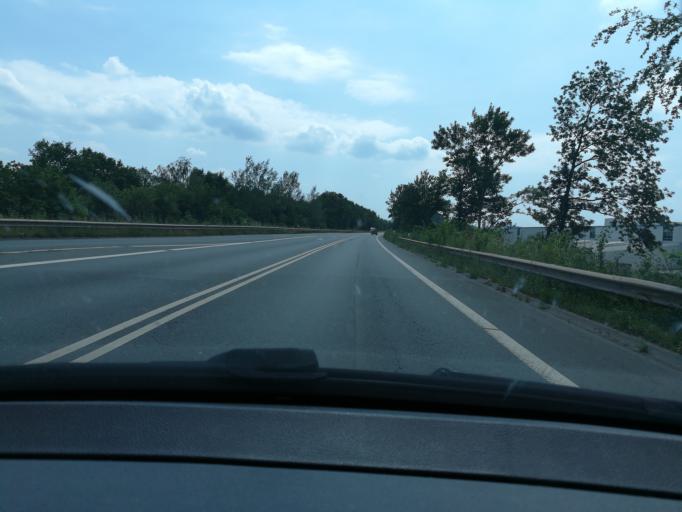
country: DE
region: North Rhine-Westphalia
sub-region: Regierungsbezirk Detmold
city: Petershagen
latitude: 52.3081
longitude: 8.9839
